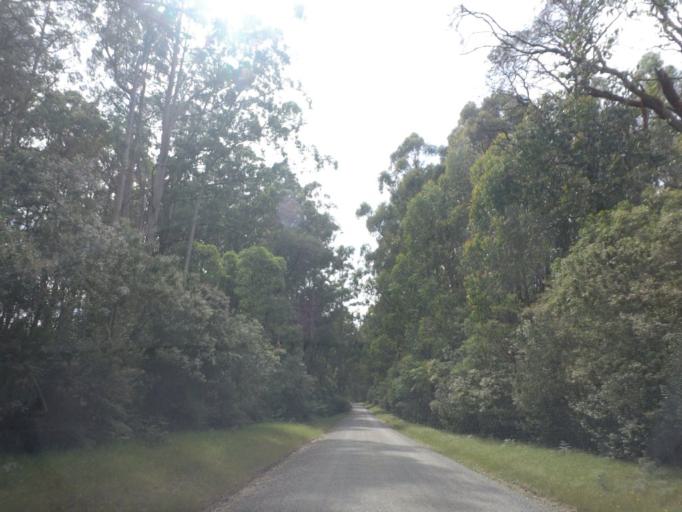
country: AU
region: Victoria
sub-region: Yarra Ranges
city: Healesville
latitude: -37.5052
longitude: 145.5194
